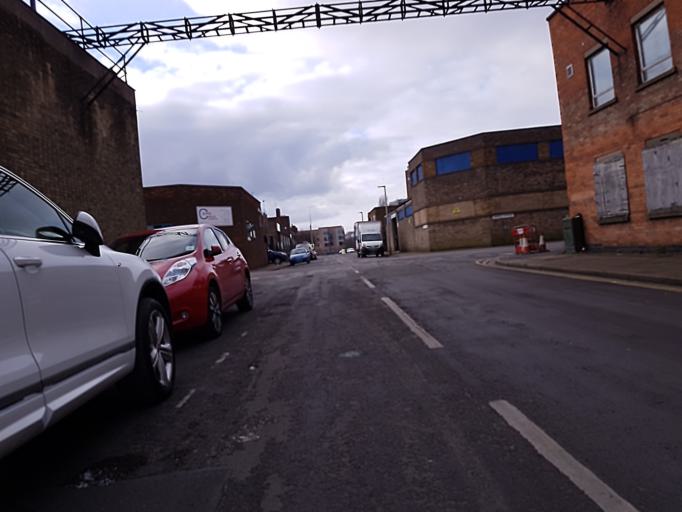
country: GB
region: England
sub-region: North East Lincolnshire
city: Grimsby
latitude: 53.5754
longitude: -0.0677
